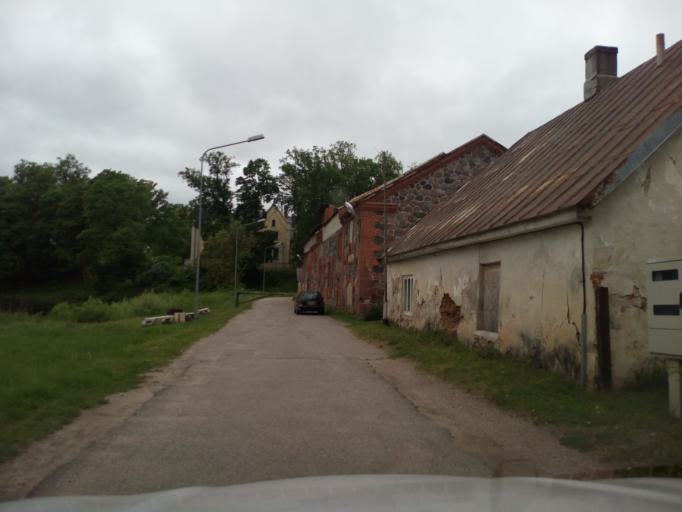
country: LV
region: Krimulda
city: Ragana
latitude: 57.3447
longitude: 24.6635
